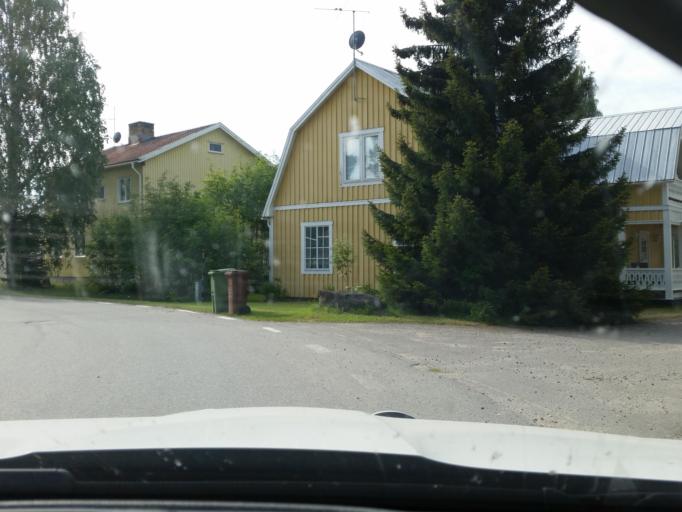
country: SE
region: Norrbotten
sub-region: Alvsbyns Kommun
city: AElvsbyn
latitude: 65.6677
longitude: 20.8662
